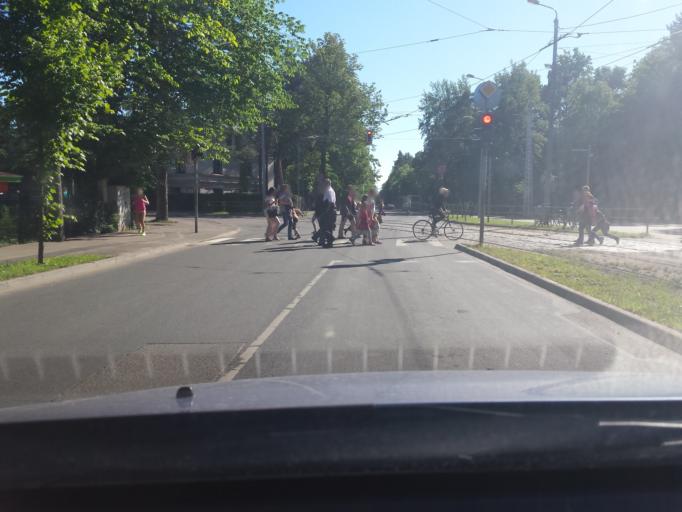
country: LV
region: Riga
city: Jaunciems
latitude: 57.0054
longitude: 24.1574
